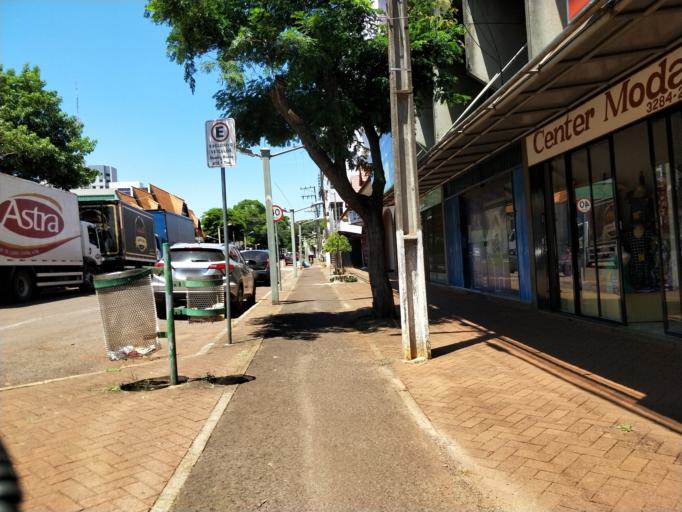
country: BR
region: Parana
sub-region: Marechal Candido Rondon
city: Marechal Candido Rondon
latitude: -24.5593
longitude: -54.0602
